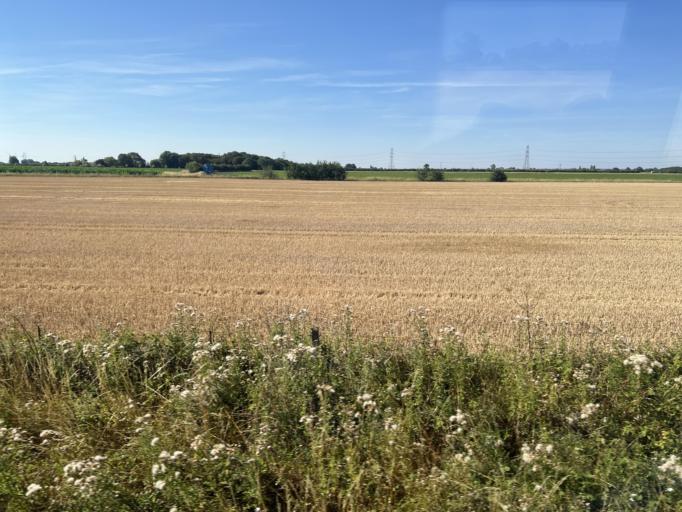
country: GB
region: England
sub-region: Lincolnshire
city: Heckington
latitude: 52.9691
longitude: -0.2491
